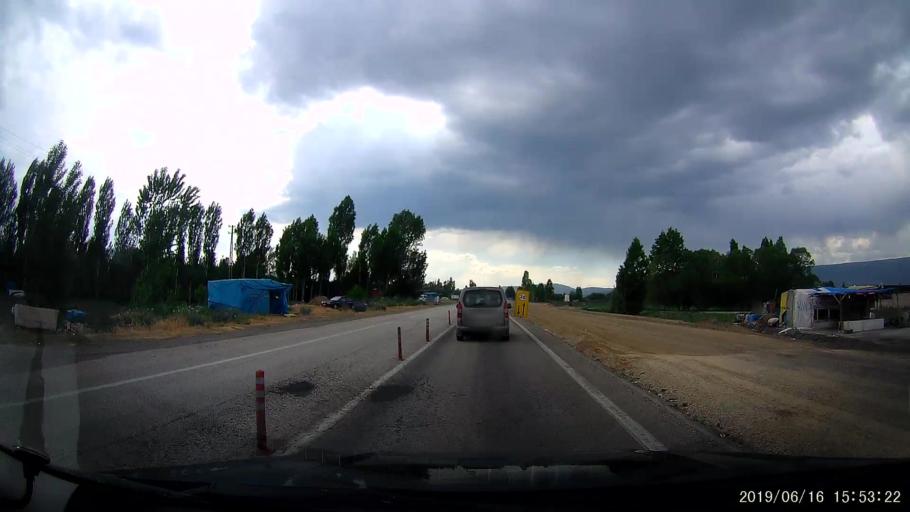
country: TR
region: Erzurum
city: Pasinler
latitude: 39.9775
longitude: 41.6477
